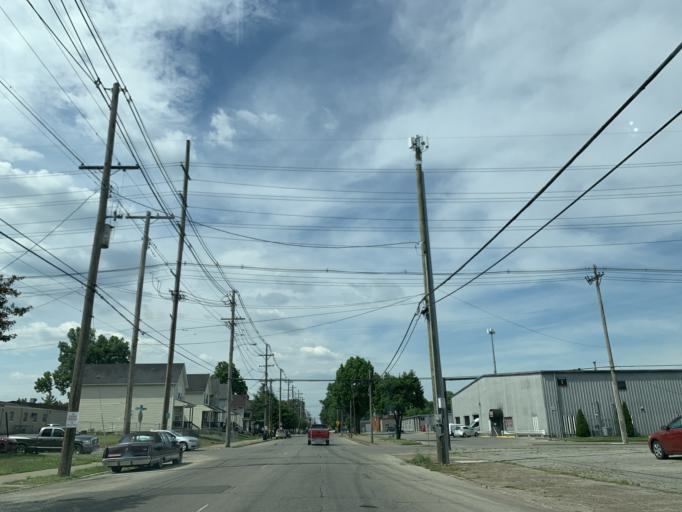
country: US
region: Kentucky
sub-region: Jefferson County
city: Louisville
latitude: 38.2492
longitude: -85.7764
